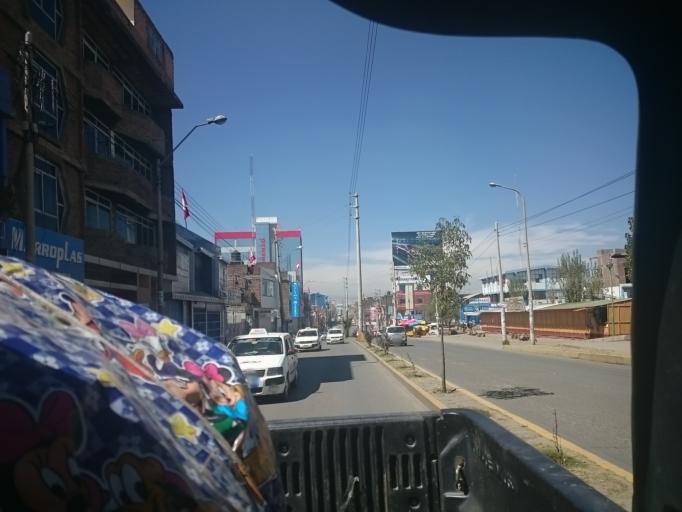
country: PE
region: Junin
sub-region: Provincia de Huancayo
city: El Tambo
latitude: -12.0480
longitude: -75.2231
